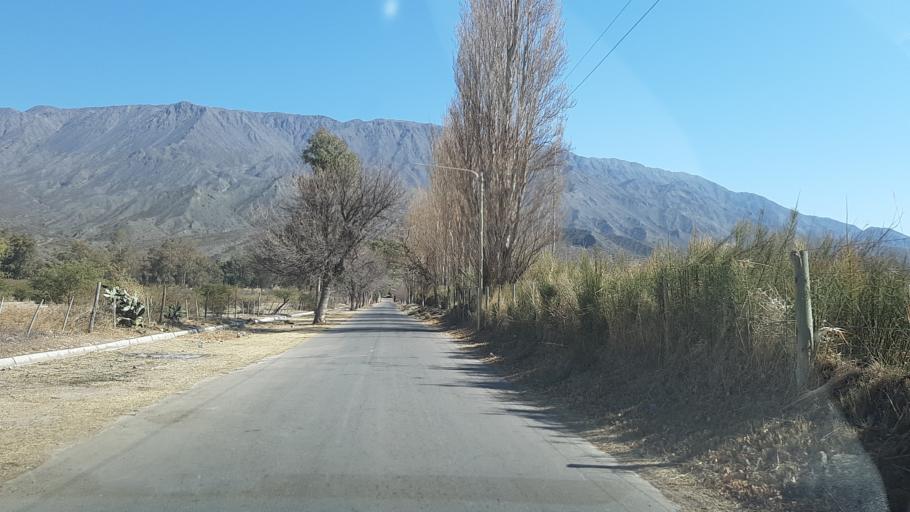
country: AR
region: San Juan
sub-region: Departamento de Zonda
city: Zonda
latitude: -31.5712
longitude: -68.7516
